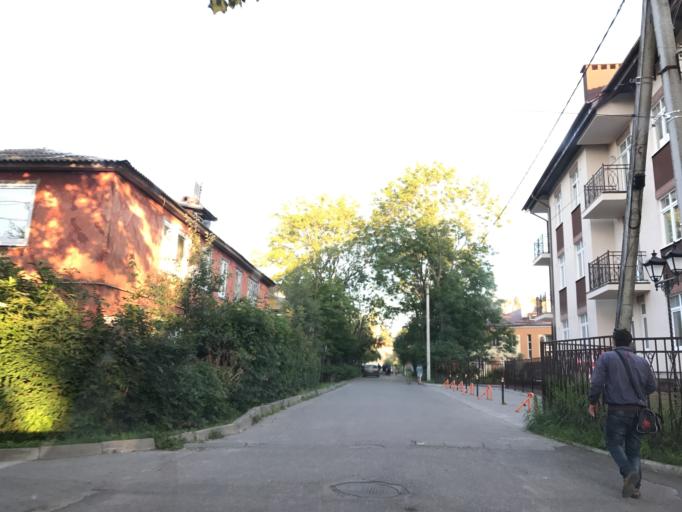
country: RU
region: Kaliningrad
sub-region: Zelenogradskiy Rayon
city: Zelenogradsk
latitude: 54.9575
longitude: 20.4652
